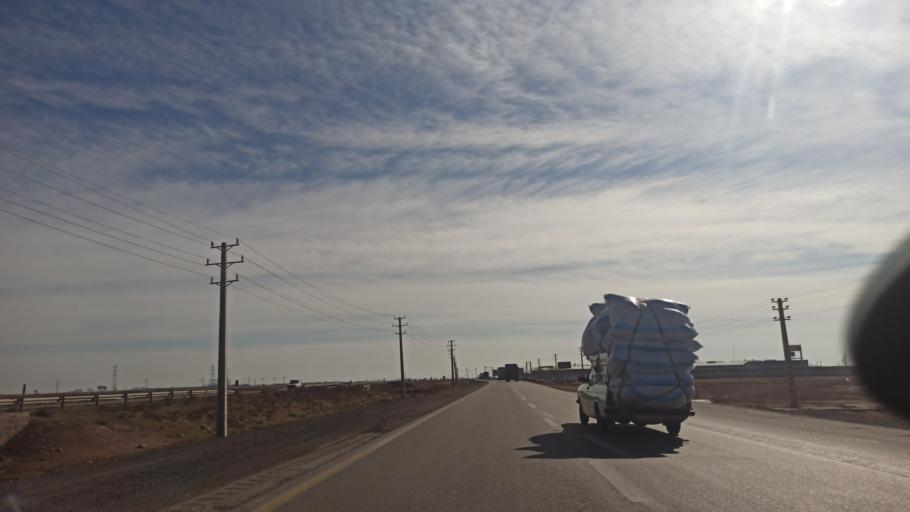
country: IR
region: Qazvin
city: Alvand
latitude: 36.0949
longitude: 50.0455
